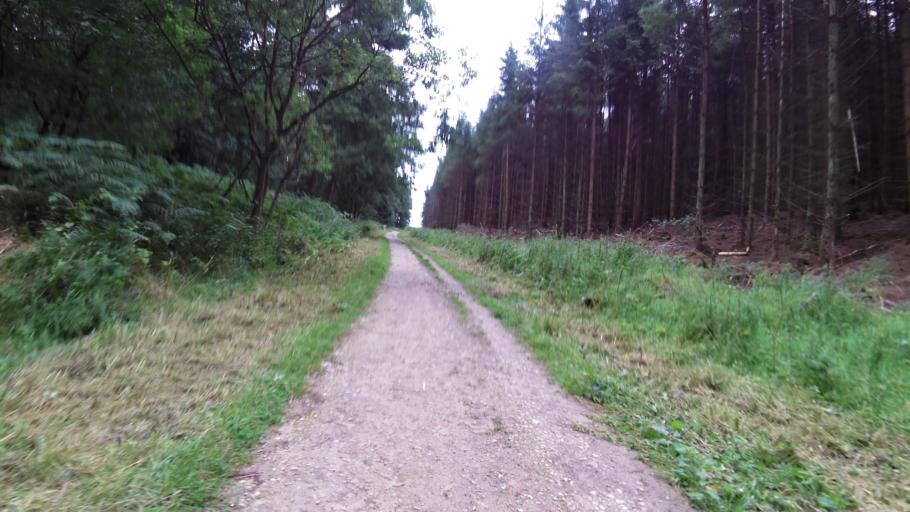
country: GB
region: England
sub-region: North Yorkshire
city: Thornton Dale
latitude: 54.2844
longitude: -0.6739
